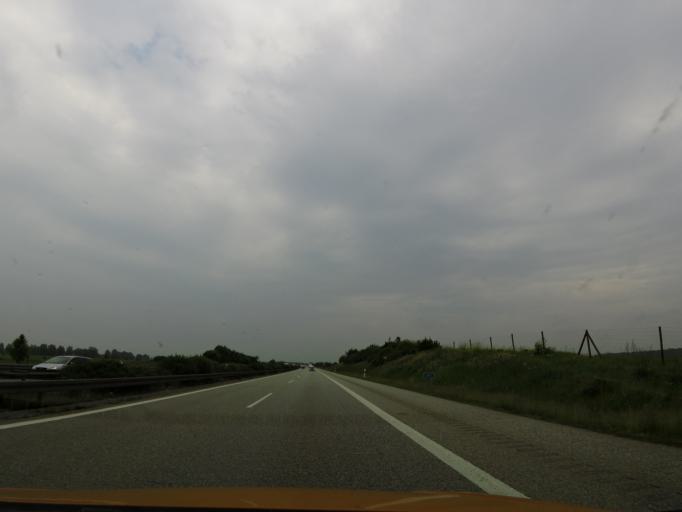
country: DE
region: Mecklenburg-Vorpommern
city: Grevesmuhlen
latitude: 53.8200
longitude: 11.1409
